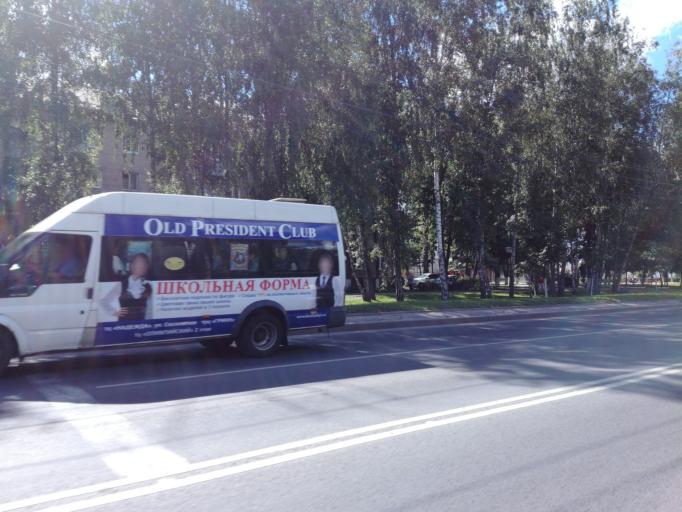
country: RU
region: Kursk
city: Kursk
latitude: 51.7710
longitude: 36.1807
